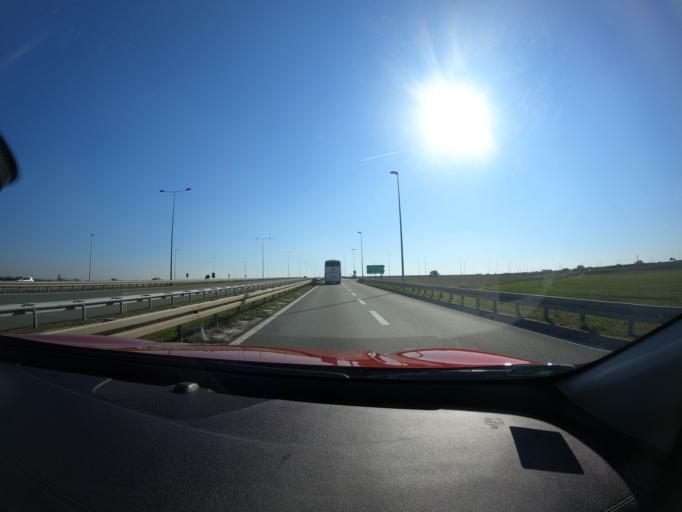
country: RS
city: Dobanovci
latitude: 44.8405
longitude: 20.2490
